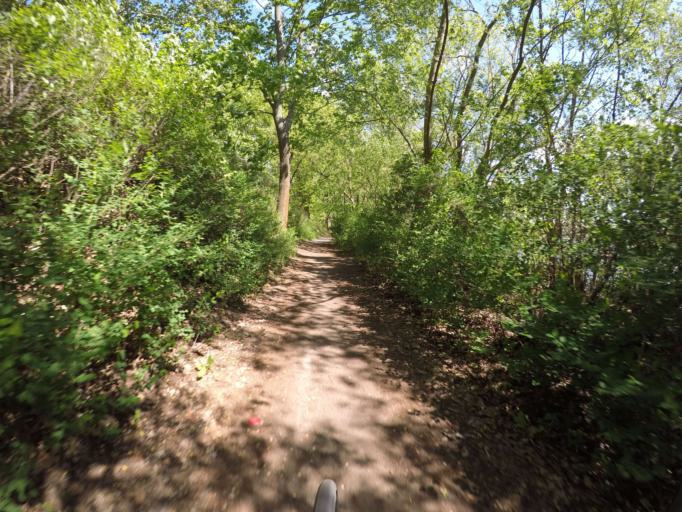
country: DE
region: Brandenburg
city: Werder
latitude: 52.3926
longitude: 12.9381
